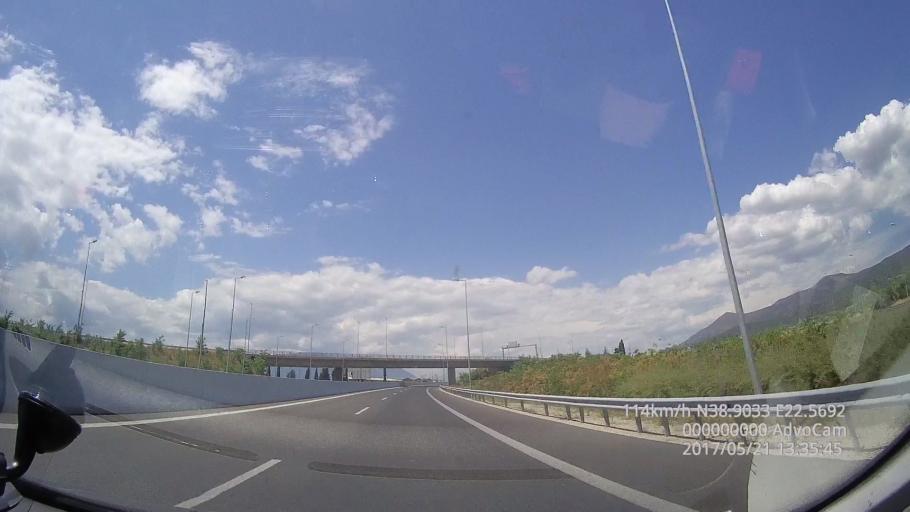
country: GR
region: Central Greece
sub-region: Nomos Fthiotidos
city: Stylida
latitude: 38.9032
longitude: 22.5687
